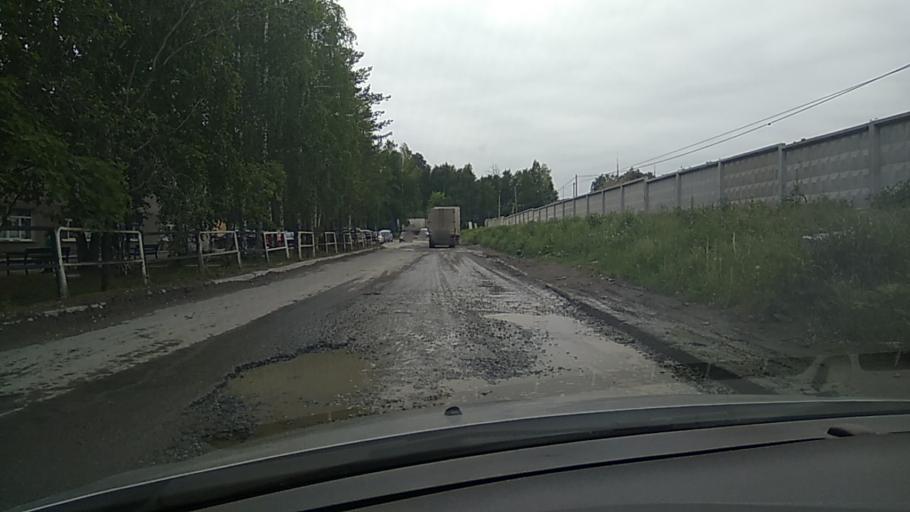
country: RU
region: Sverdlovsk
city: Shuvakish
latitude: 56.8939
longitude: 60.5173
